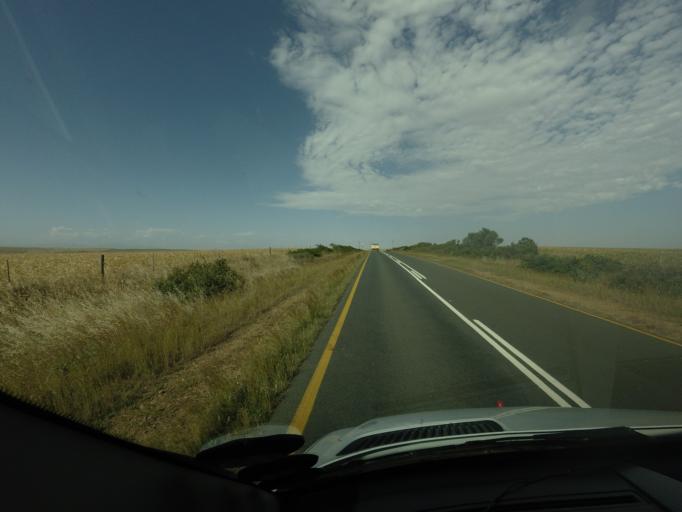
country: ZA
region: Western Cape
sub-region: Overberg District Municipality
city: Caledon
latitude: -34.3366
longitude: 19.7074
